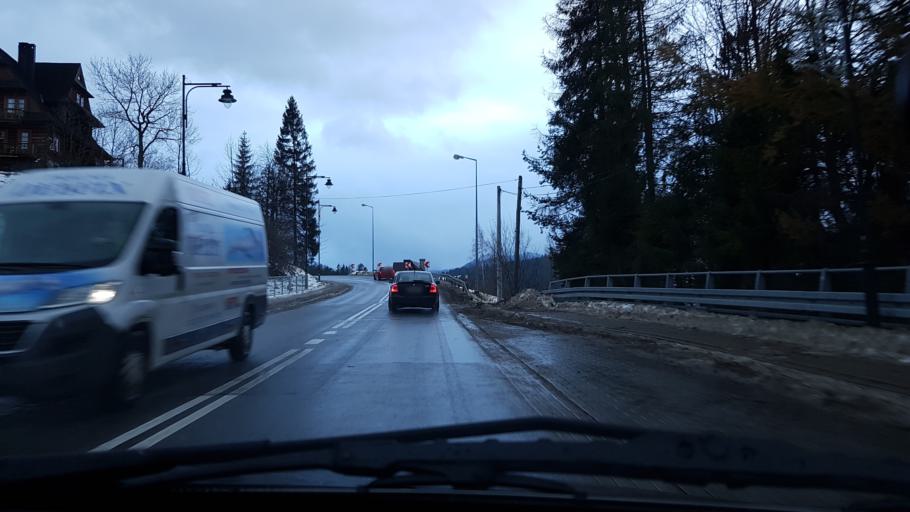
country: PL
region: Lesser Poland Voivodeship
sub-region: Powiat tatrzanski
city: Bukowina Tatrzanska
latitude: 49.3278
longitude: 20.0985
